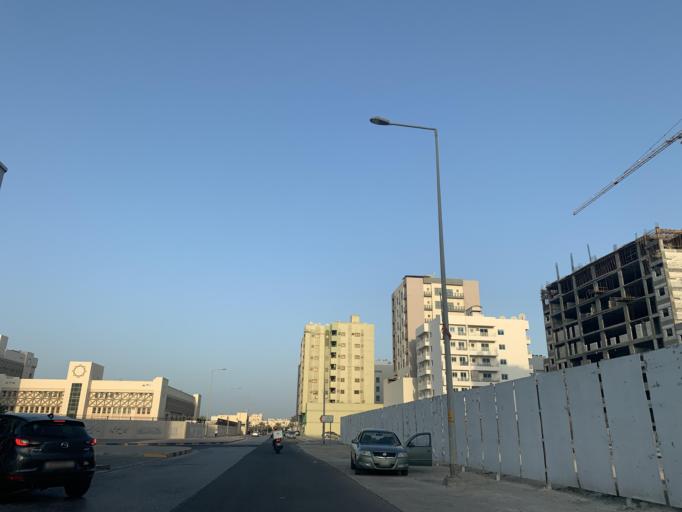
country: BH
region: Muharraq
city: Al Muharraq
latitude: 26.2650
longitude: 50.5993
